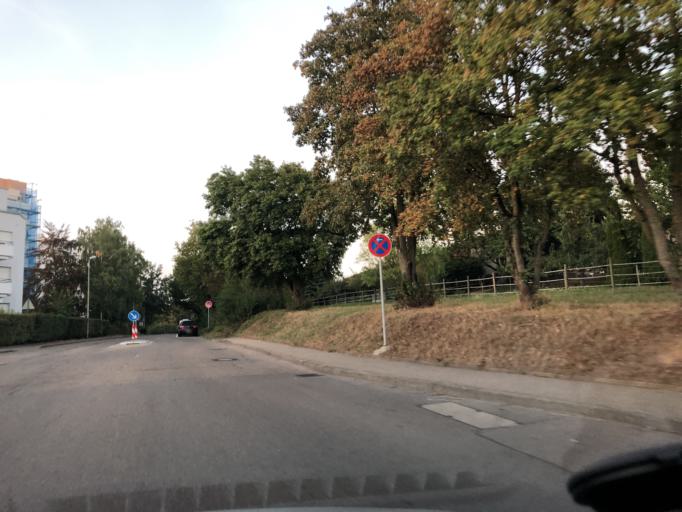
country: DE
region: Baden-Wuerttemberg
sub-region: Regierungsbezirk Stuttgart
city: Waiblingen
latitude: 48.8724
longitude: 9.2792
